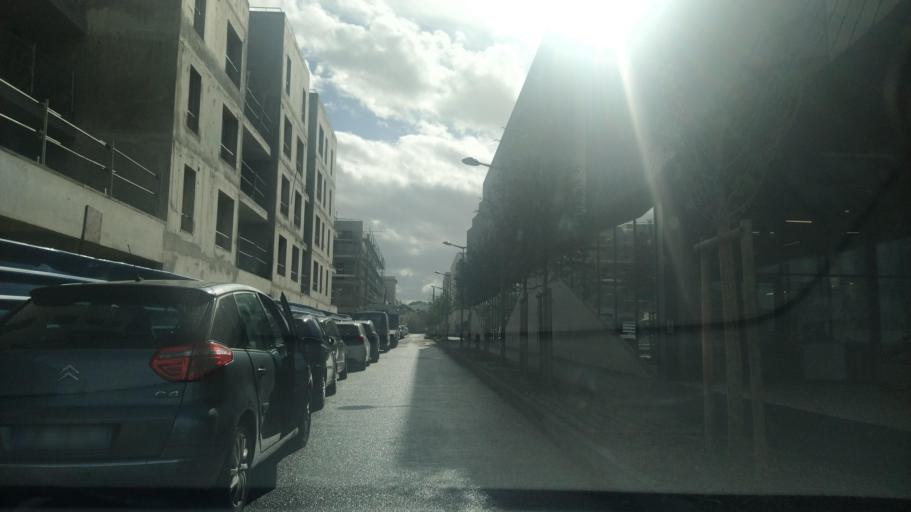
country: FR
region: Ile-de-France
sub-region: Departement des Yvelines
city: Saint-Cyr-l'Ecole
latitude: 48.8096
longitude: 2.0625
